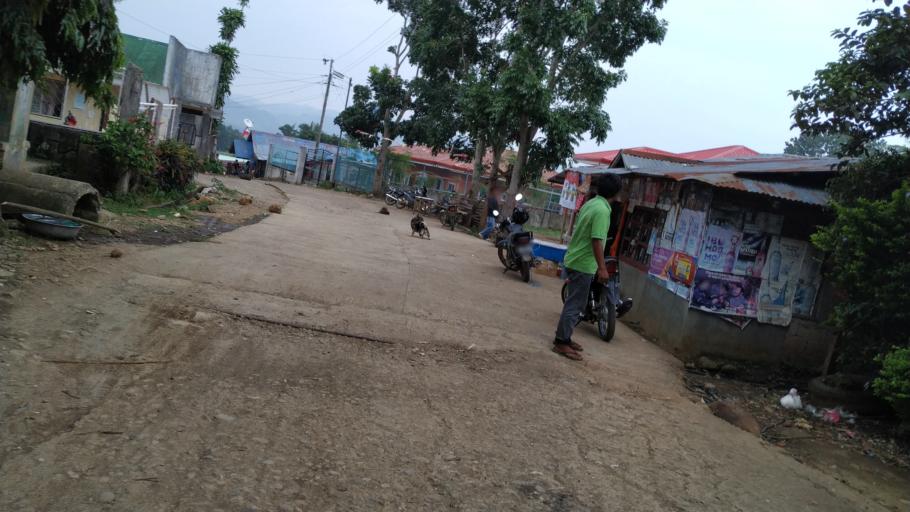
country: PH
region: Western Visayas
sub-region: Province of Negros Occidental
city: Quezon
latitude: 10.4240
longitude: 123.2324
